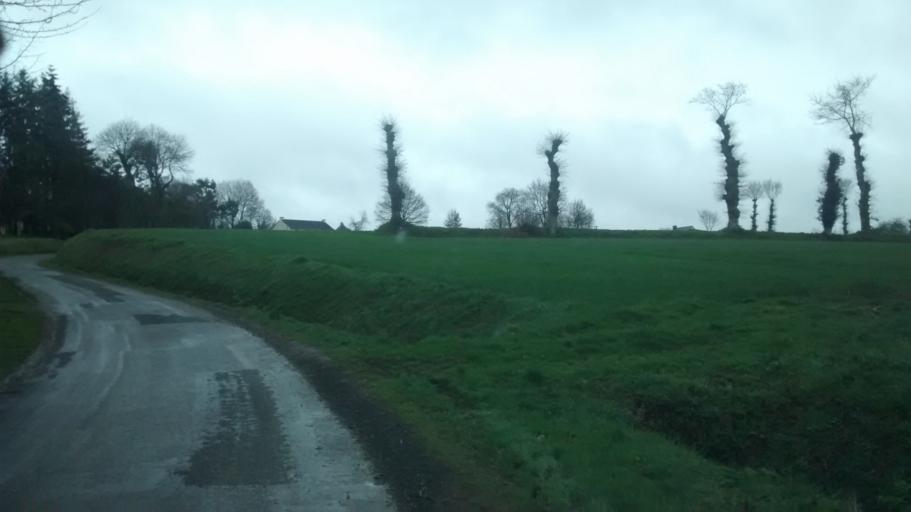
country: FR
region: Brittany
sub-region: Departement d'Ille-et-Vilaine
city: Melesse
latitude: 48.2065
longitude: -1.6747
